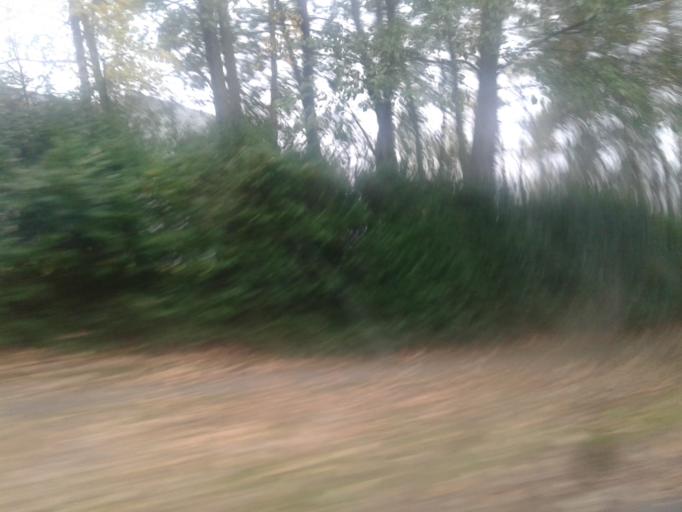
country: IE
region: Leinster
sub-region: Fingal County
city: Blanchardstown
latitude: 53.4096
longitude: -6.3596
